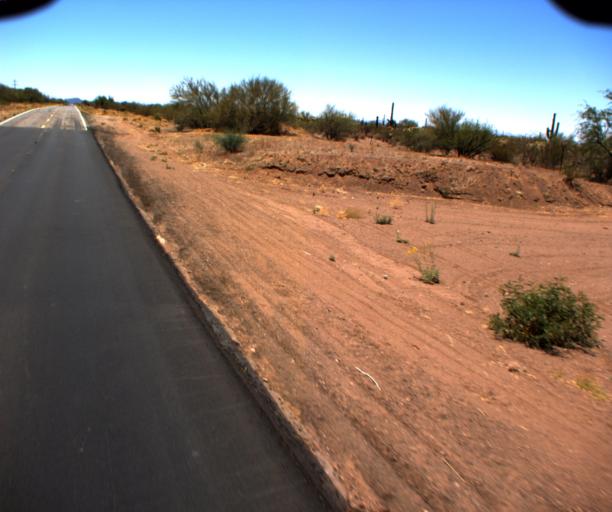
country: US
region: Arizona
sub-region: Pima County
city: Sells
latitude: 32.0703
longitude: -112.0416
